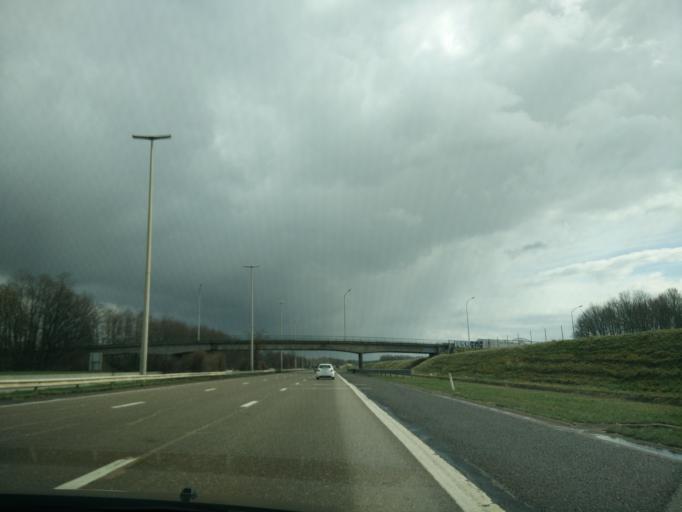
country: BE
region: Wallonia
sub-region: Province de Liege
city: Oreye
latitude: 50.7022
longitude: 5.3334
